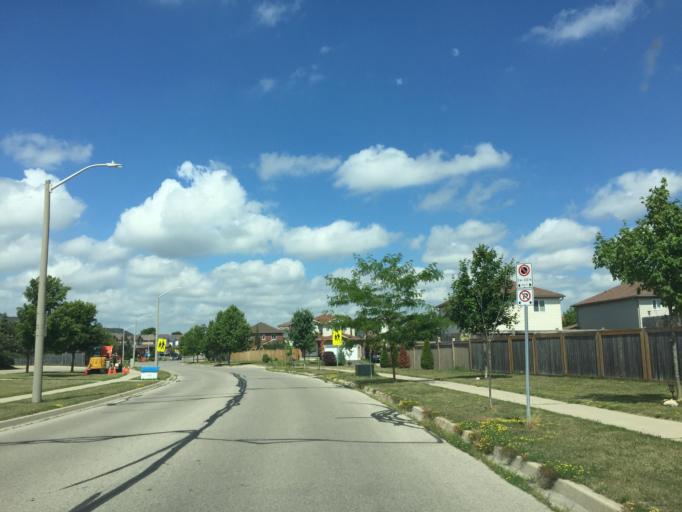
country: CA
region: Ontario
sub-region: Wellington County
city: Guelph
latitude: 43.5199
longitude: -80.1849
